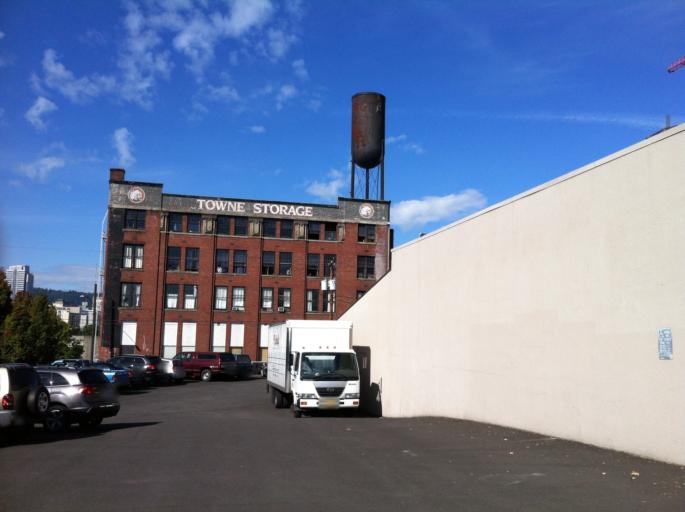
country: US
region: Oregon
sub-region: Multnomah County
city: Portland
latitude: 45.5224
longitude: -122.6620
